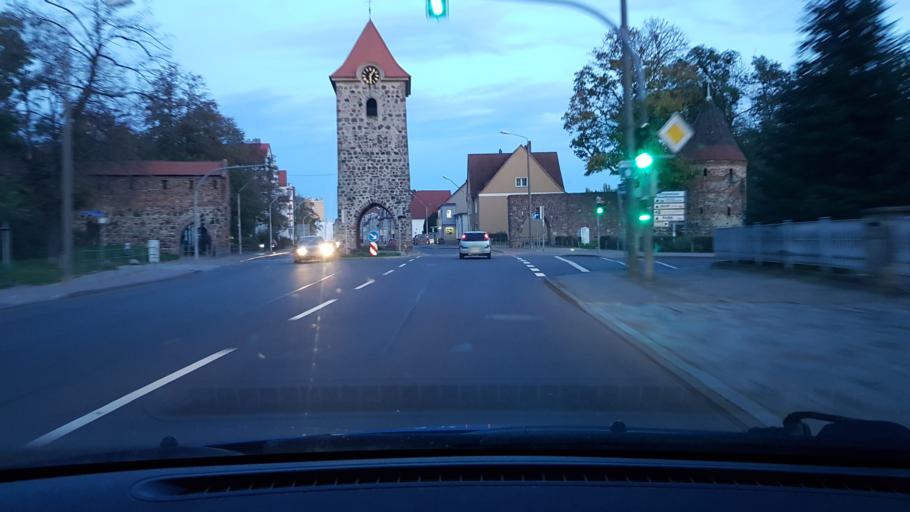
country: DE
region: Saxony-Anhalt
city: Zerbst
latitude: 51.9670
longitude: 12.0773
